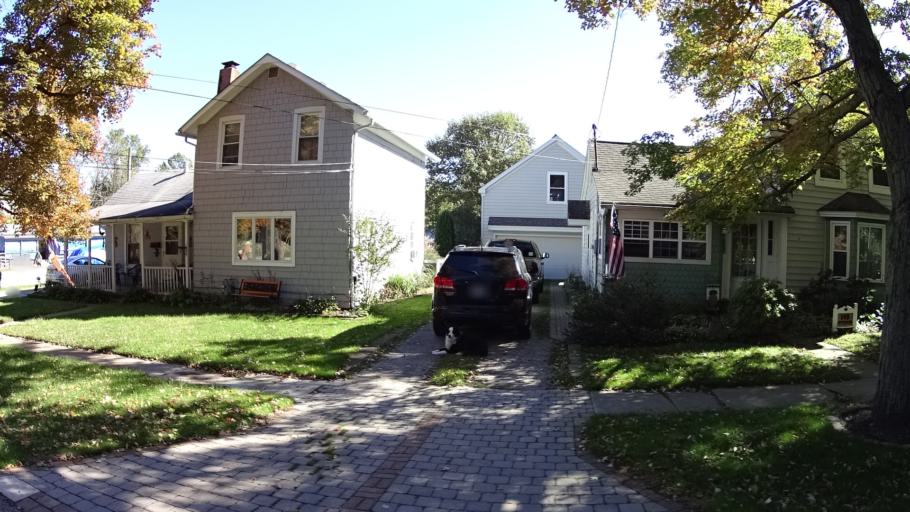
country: US
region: Ohio
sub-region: Lorain County
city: Amherst
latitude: 41.3994
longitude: -82.2419
